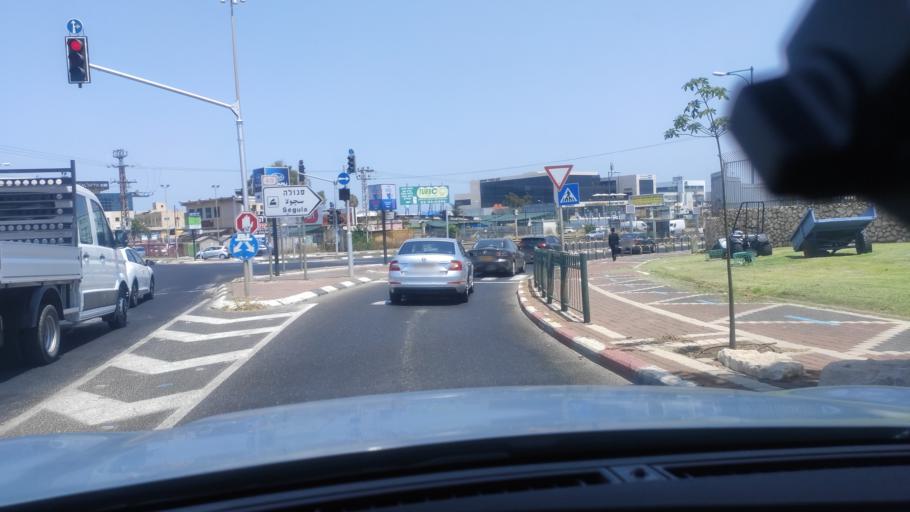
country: IL
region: Central District
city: Petah Tiqwa
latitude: 32.1017
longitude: 34.8983
